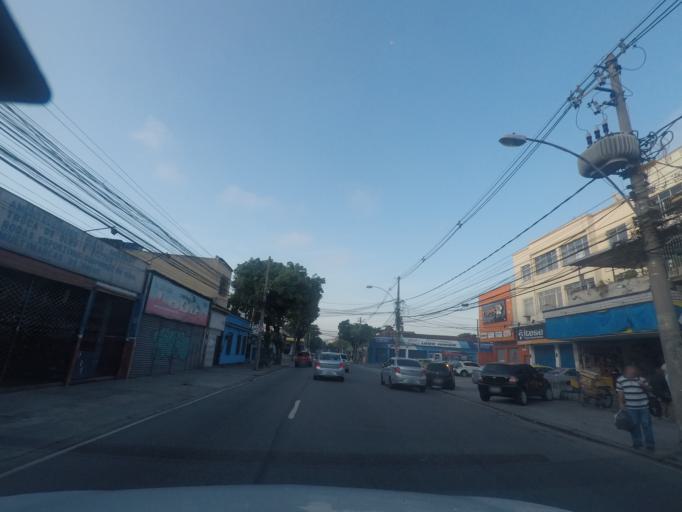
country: BR
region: Rio de Janeiro
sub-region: Duque De Caxias
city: Duque de Caxias
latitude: -22.8294
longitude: -43.2770
